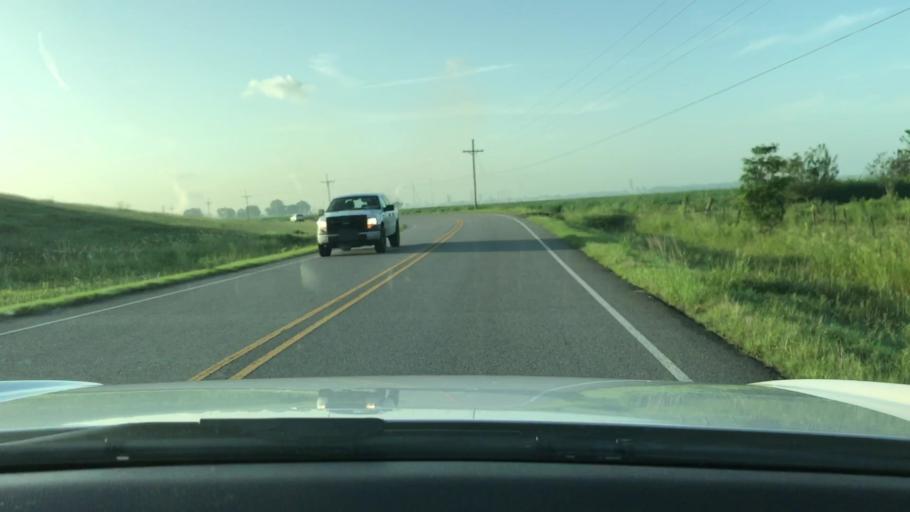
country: US
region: Louisiana
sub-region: Iberville Parish
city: Plaquemine
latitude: 30.2750
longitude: -91.2085
